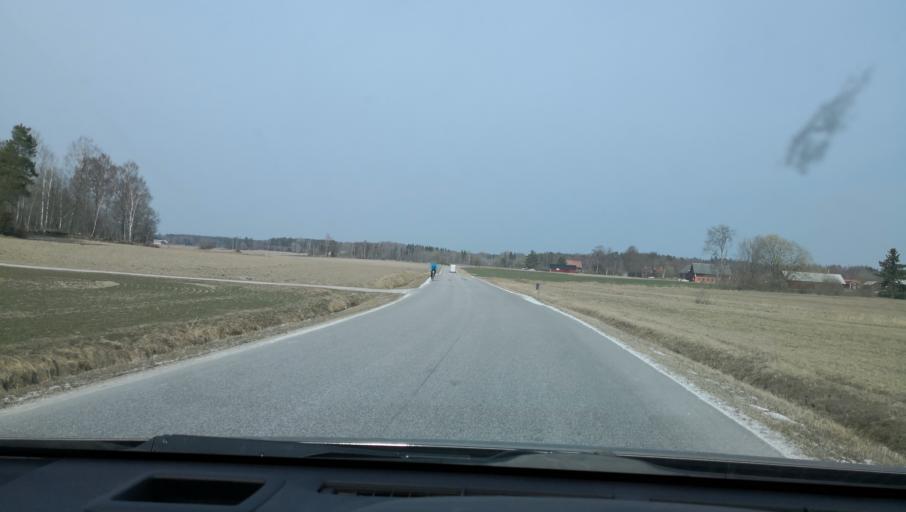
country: SE
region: OErebro
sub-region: Lindesbergs Kommun
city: Frovi
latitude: 59.3339
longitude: 15.4433
